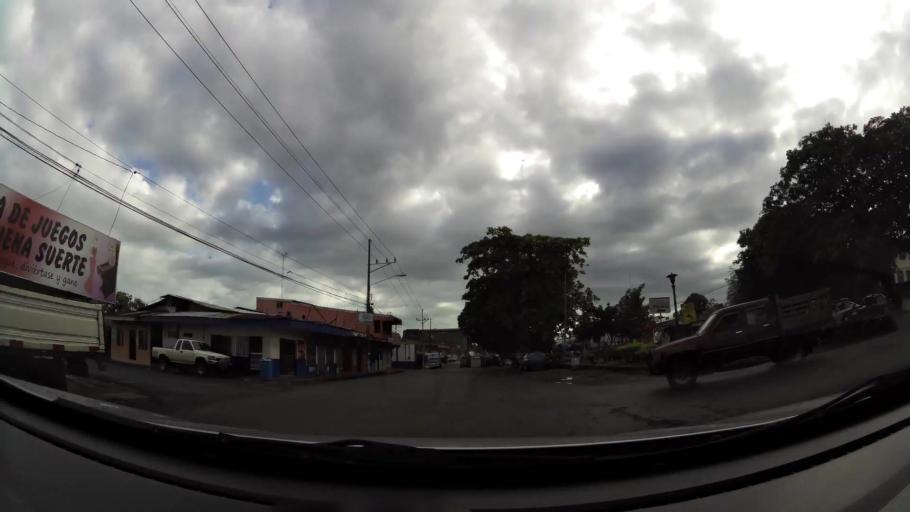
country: CR
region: Limon
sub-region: Canton de Pococi
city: Guapiles
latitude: 10.2139
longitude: -83.7921
